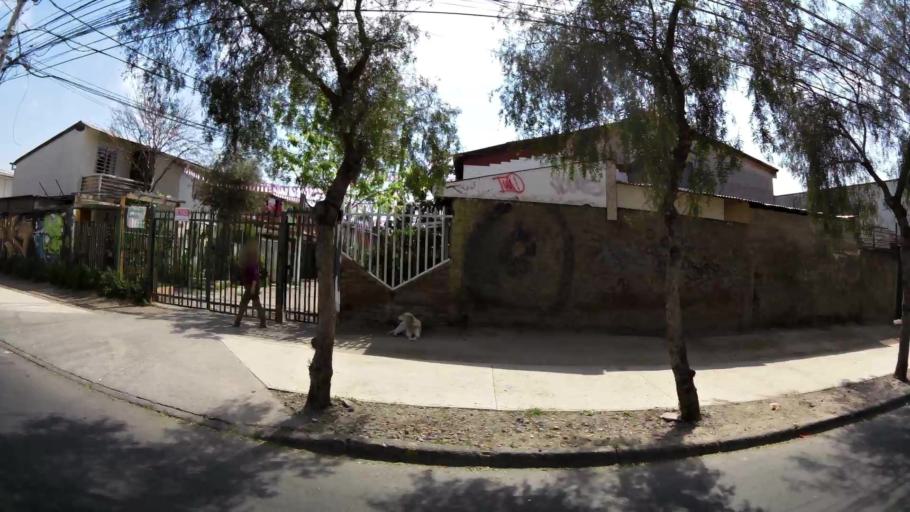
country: CL
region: Santiago Metropolitan
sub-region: Provincia de Cordillera
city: Puente Alto
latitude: -33.5880
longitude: -70.5994
